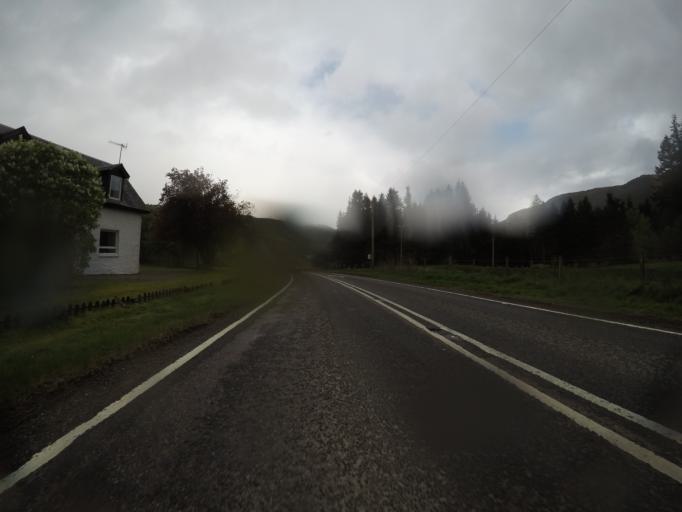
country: GB
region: Scotland
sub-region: Highland
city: Spean Bridge
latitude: 57.0347
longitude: -4.8126
